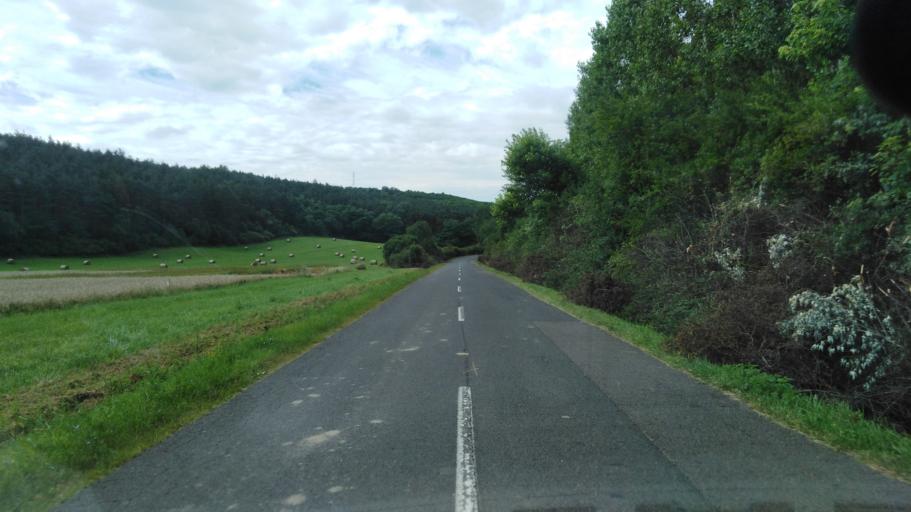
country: HU
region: Nograd
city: Karancskeszi
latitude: 48.2248
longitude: 19.6136
